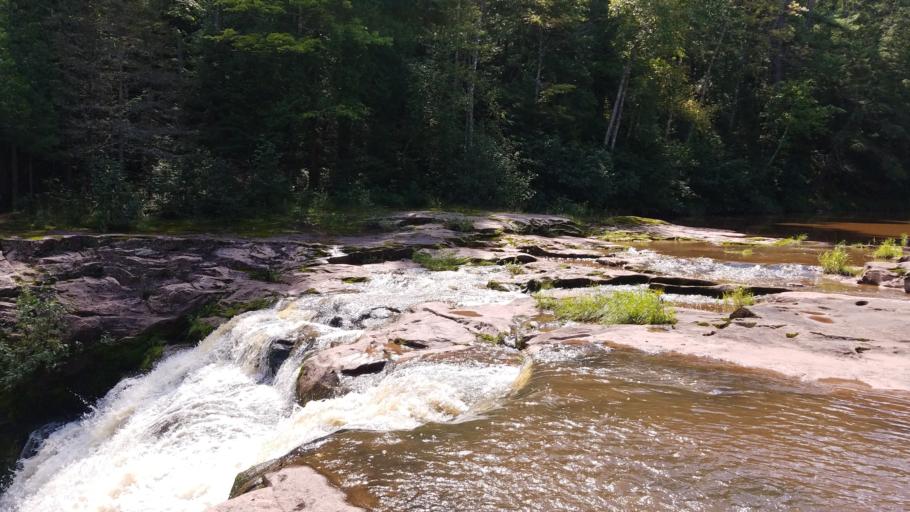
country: US
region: Michigan
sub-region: Ontonagon County
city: Ontonagon
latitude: 46.6513
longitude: -89.1525
